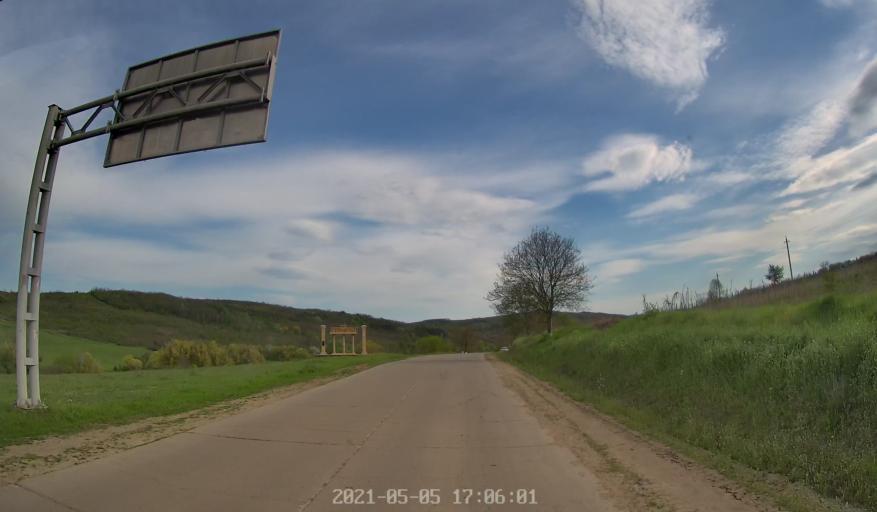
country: MD
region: Chisinau
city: Vadul lui Voda
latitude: 47.0243
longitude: 29.1402
